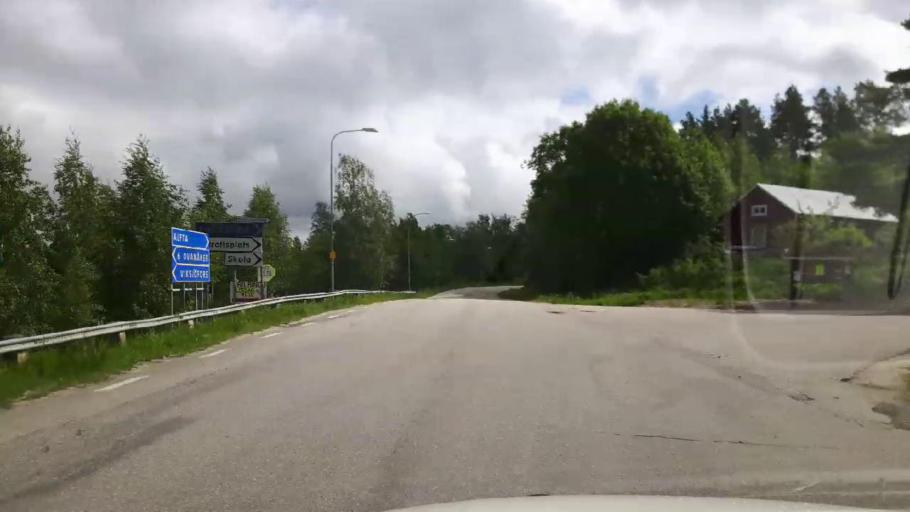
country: SE
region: Gaevleborg
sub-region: Ovanakers Kommun
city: Alfta
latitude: 61.3360
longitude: 15.9648
